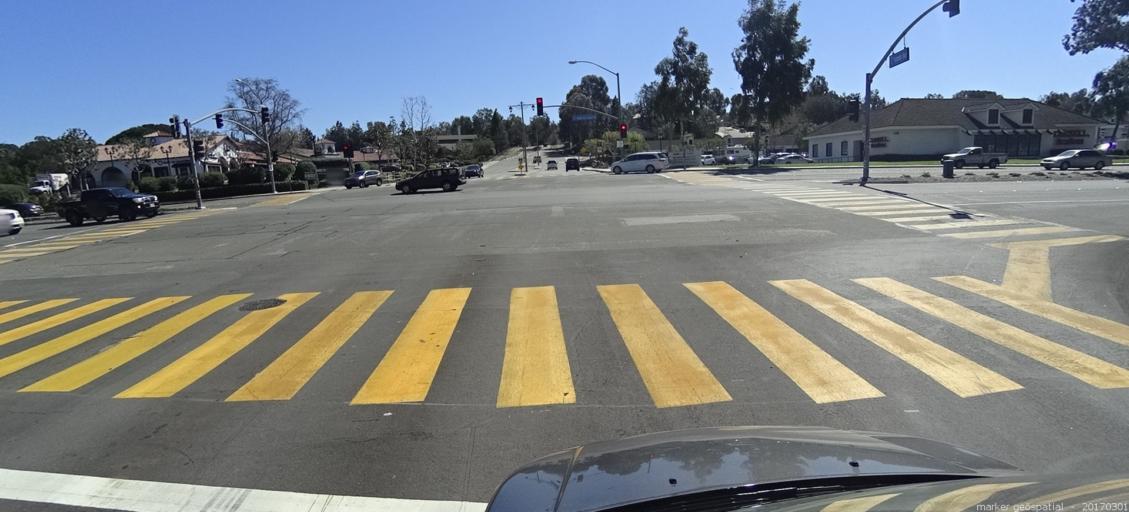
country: US
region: California
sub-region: Orange County
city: Yorba Linda
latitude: 33.8579
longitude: -117.7709
